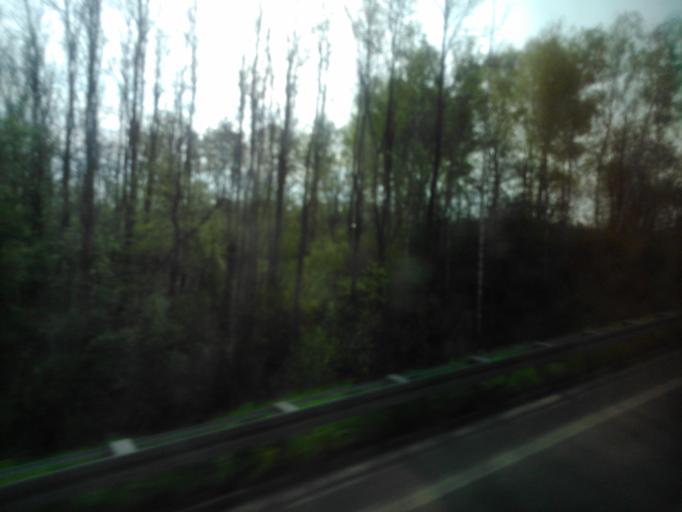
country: PL
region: Lesser Poland Voivodeship
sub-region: Powiat wielicki
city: Czarnochowice
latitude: 50.0145
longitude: 20.0621
